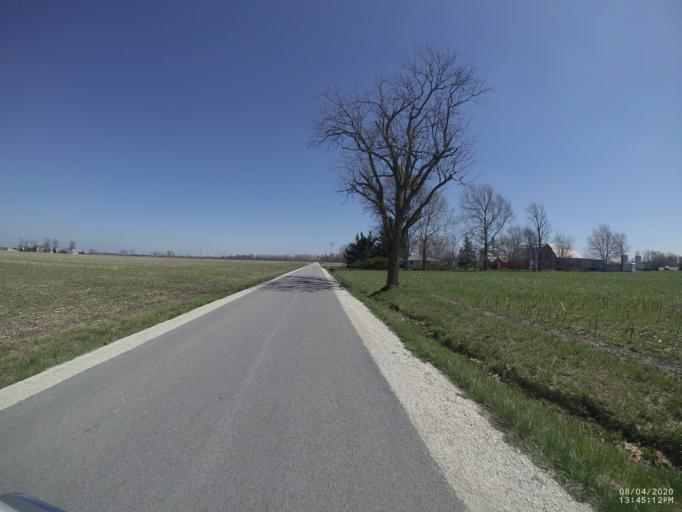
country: US
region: Ohio
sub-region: Sandusky County
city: Gibsonburg
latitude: 41.3265
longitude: -83.2952
